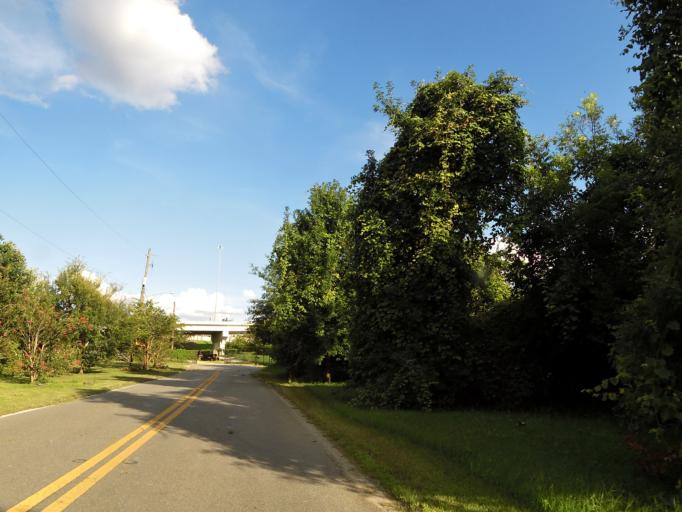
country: US
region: Florida
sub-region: Duval County
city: Jacksonville
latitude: 30.3262
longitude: -81.6821
